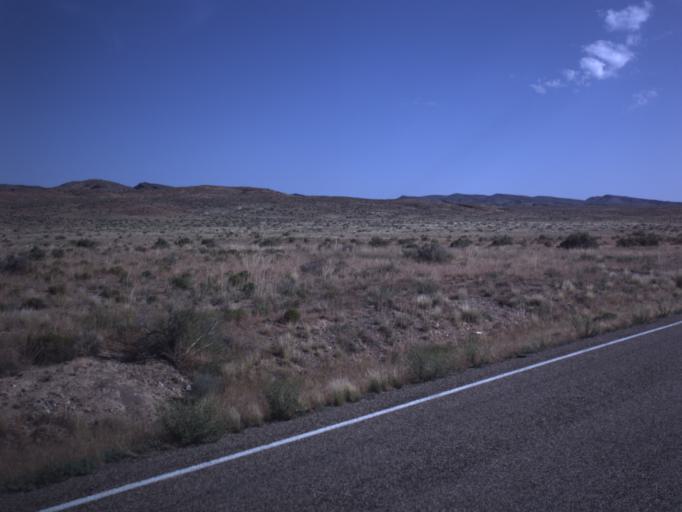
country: US
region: Utah
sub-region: Beaver County
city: Milford
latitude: 38.7502
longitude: -112.9497
